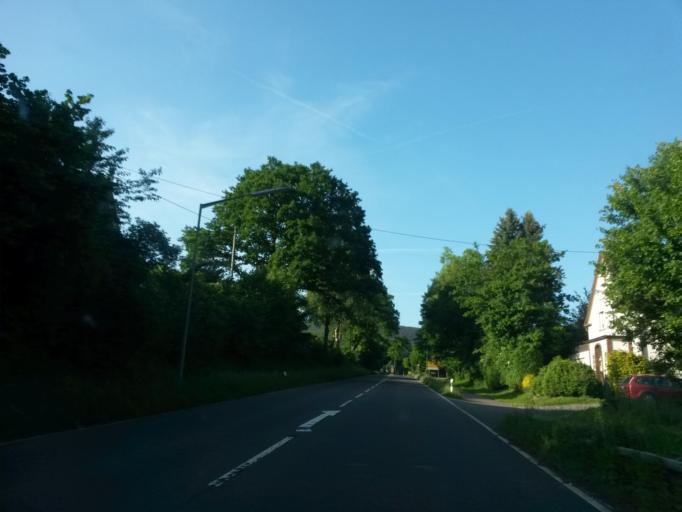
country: DE
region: North Rhine-Westphalia
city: Bergneustadt
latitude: 51.0348
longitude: 7.6941
